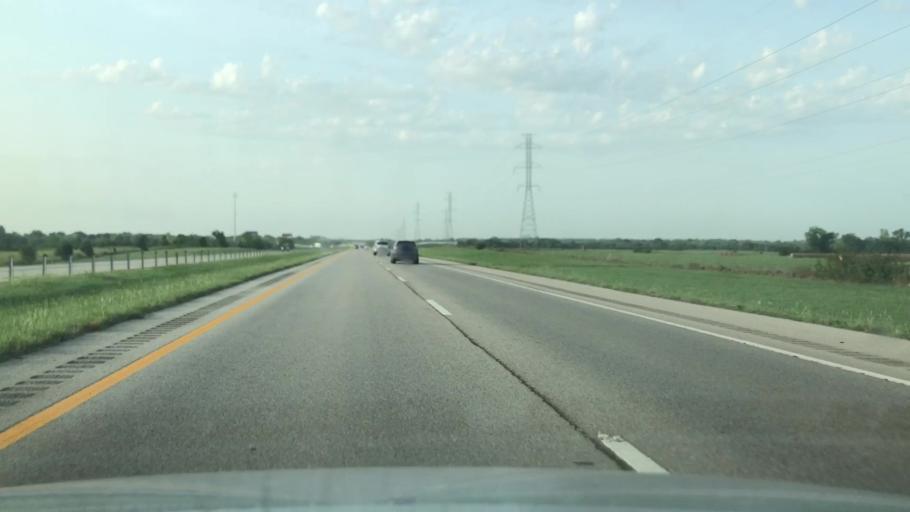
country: US
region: Oklahoma
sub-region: Tulsa County
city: Sperry
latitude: 36.3337
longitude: -95.9254
